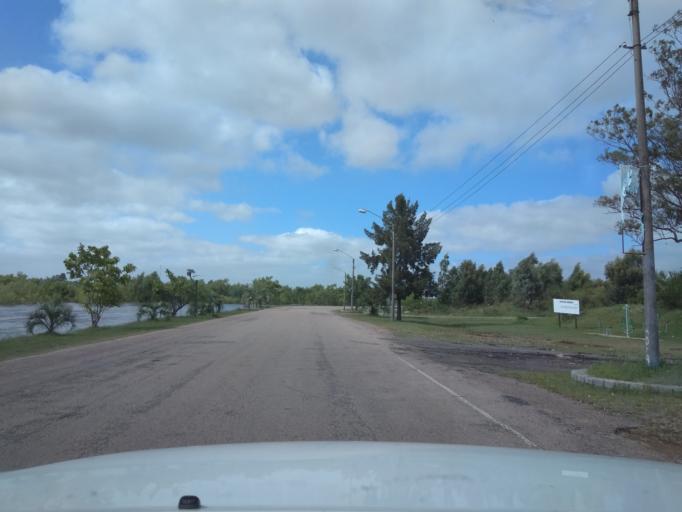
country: UY
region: Florida
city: Florida
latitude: -34.1031
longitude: -56.2038
